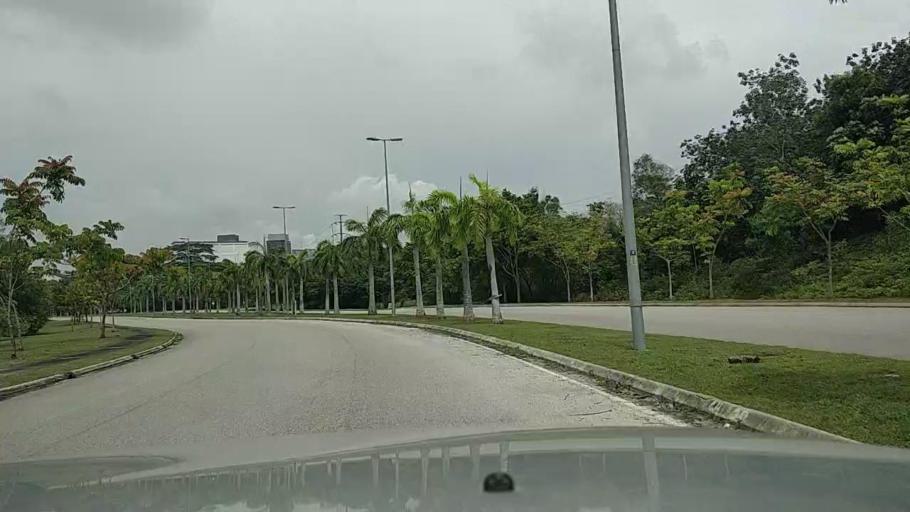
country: MY
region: Putrajaya
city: Putrajaya
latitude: 2.9026
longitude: 101.6521
